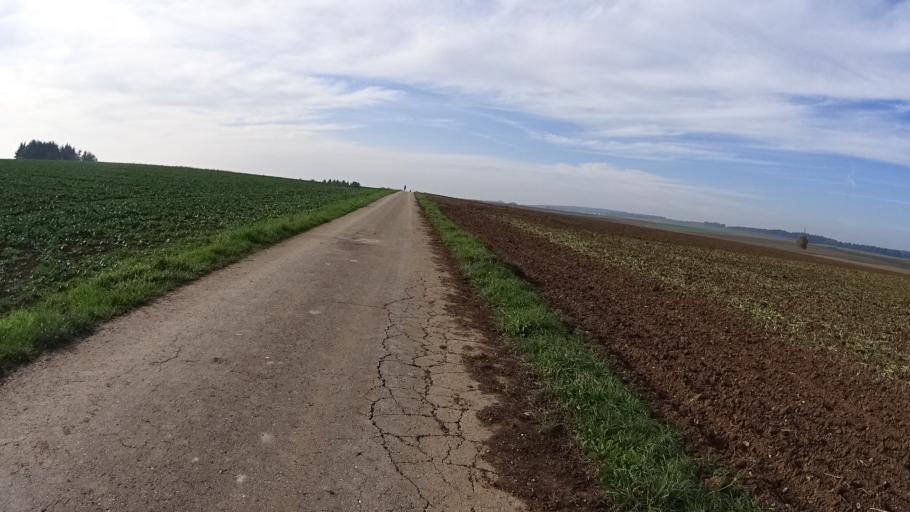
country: DE
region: Bavaria
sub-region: Upper Bavaria
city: Eitensheim
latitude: 48.8197
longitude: 11.3093
